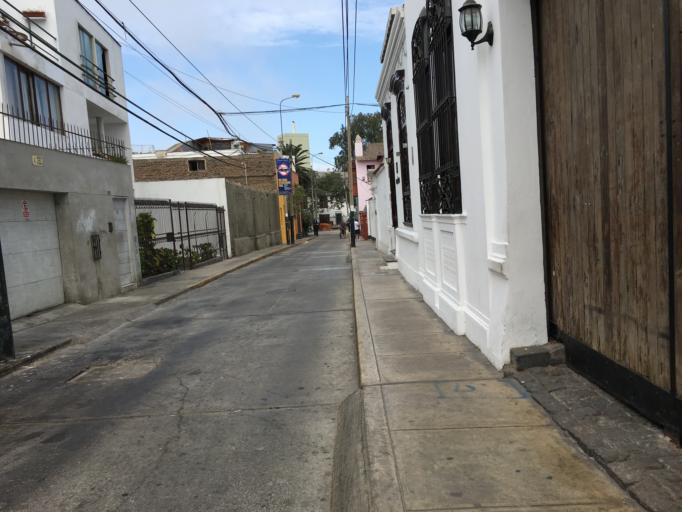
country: PE
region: Lima
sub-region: Lima
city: Surco
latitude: -12.1496
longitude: -77.0223
